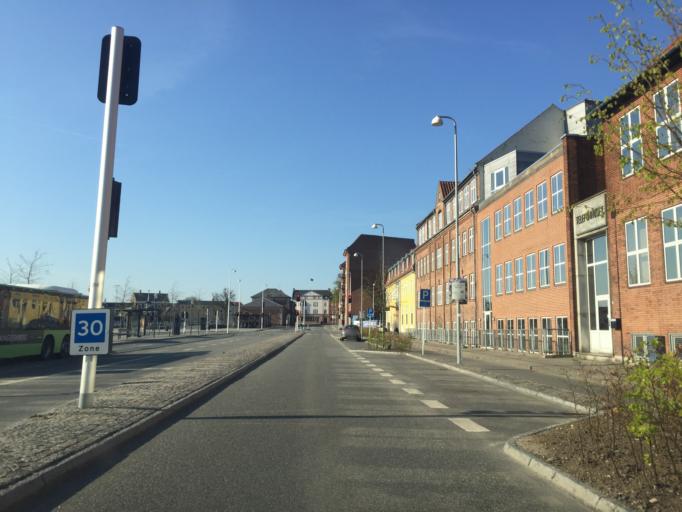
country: DK
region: South Denmark
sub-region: Svendborg Kommune
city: Svendborg
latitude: 55.0614
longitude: 10.6126
